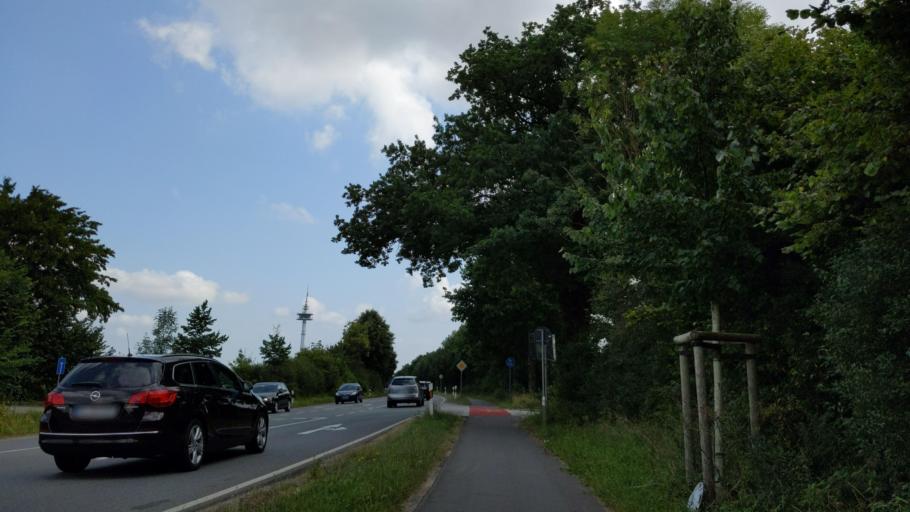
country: DE
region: Schleswig-Holstein
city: Stockelsdorf
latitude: 53.8987
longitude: 10.6326
